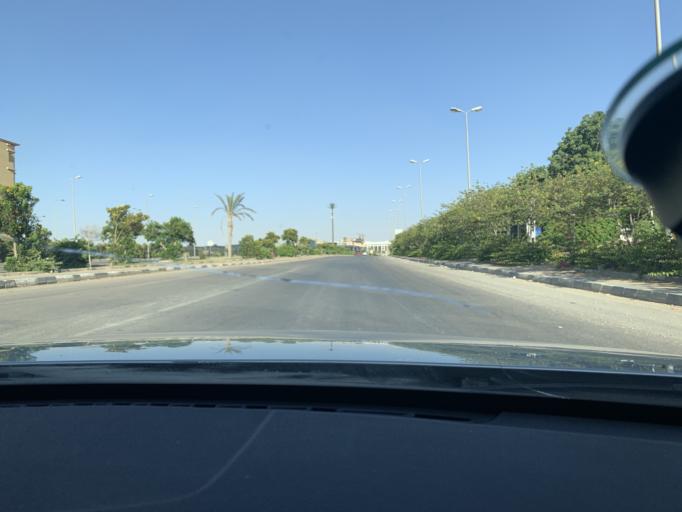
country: EG
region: Muhafazat al Qalyubiyah
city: Al Khankah
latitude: 30.0520
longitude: 31.5077
